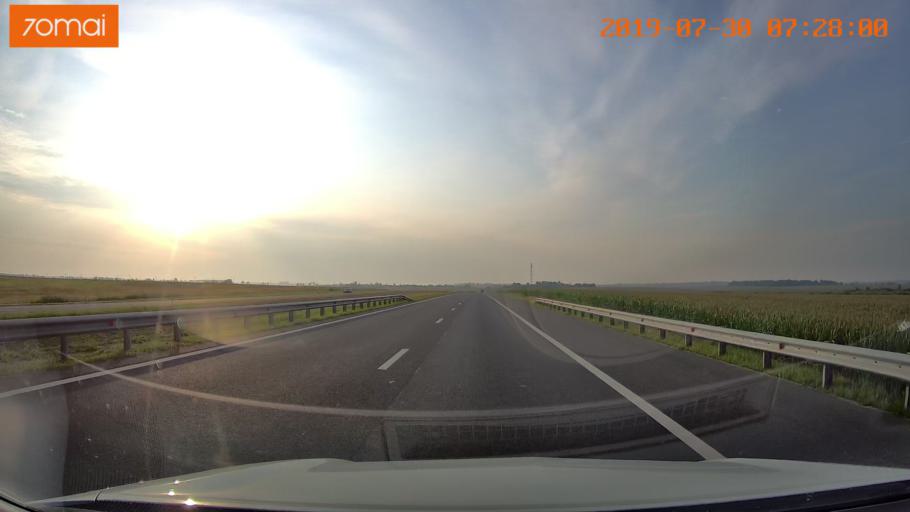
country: RU
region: Kaliningrad
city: Gvardeysk
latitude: 54.6794
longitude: 20.9017
